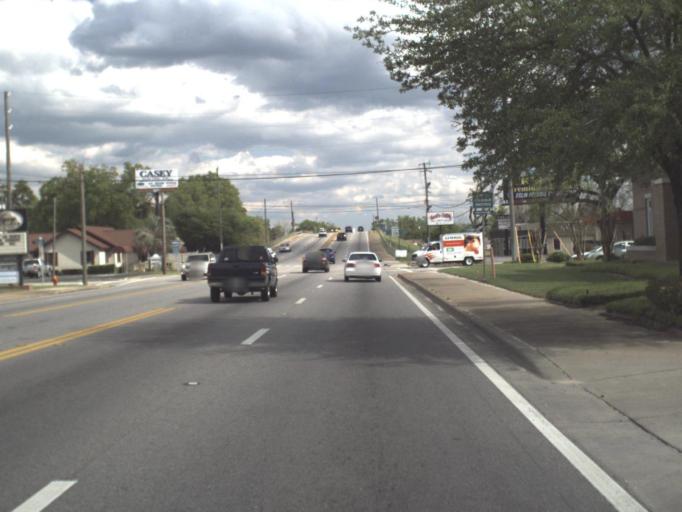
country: US
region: Florida
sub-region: Okaloosa County
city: Crestview
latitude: 30.7605
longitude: -86.5703
